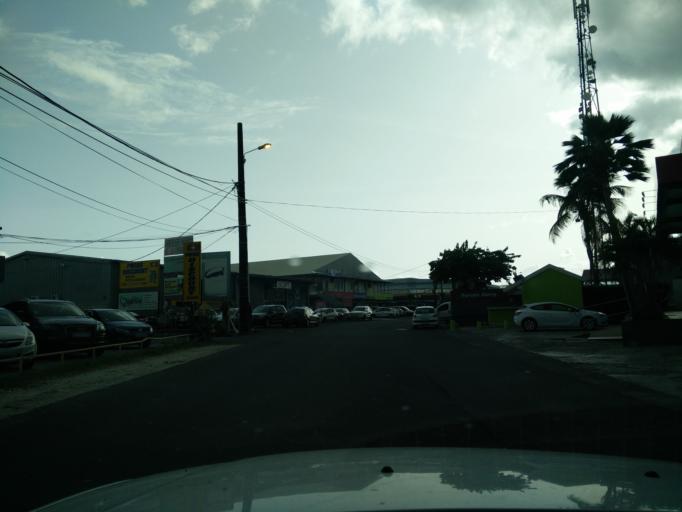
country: GP
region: Guadeloupe
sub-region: Guadeloupe
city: Pointe-a-Pitre
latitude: 16.2398
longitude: -61.5659
